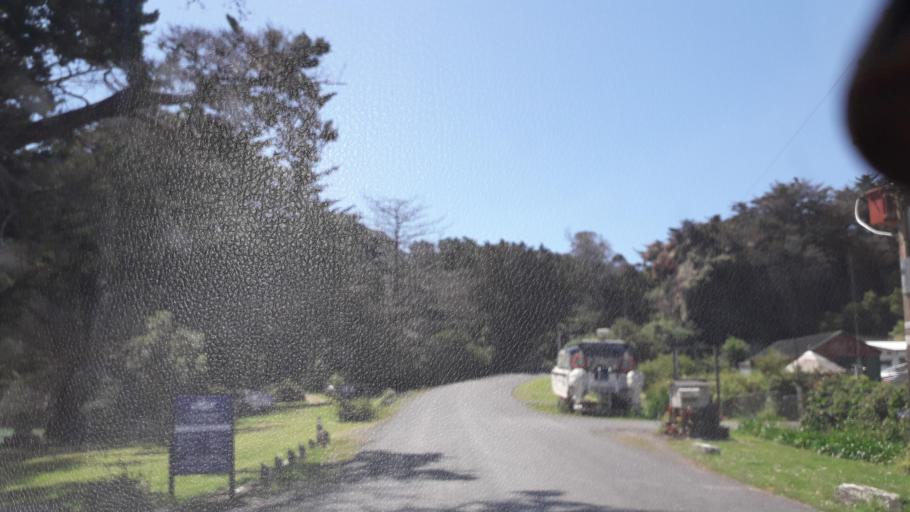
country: NZ
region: Northland
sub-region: Far North District
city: Paihia
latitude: -35.2323
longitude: 174.2608
